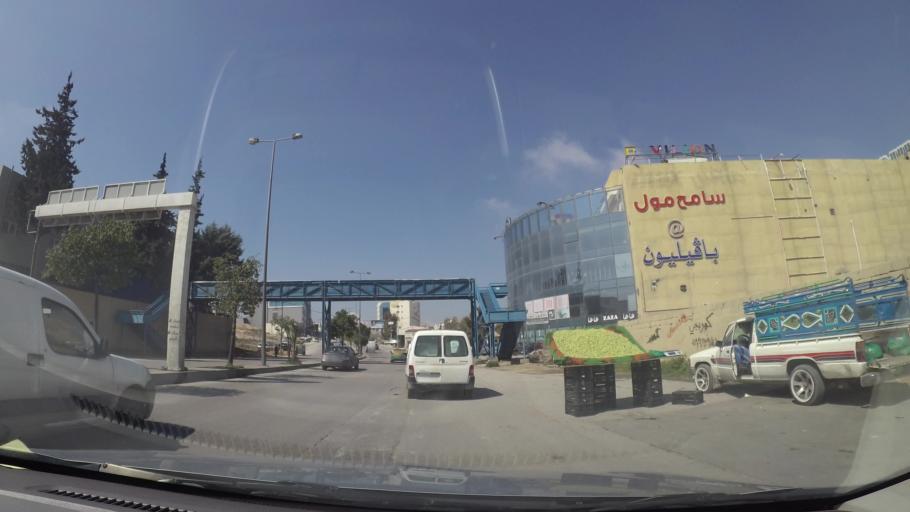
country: JO
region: Amman
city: Al Bunayyat ash Shamaliyah
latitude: 31.9177
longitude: 35.9019
